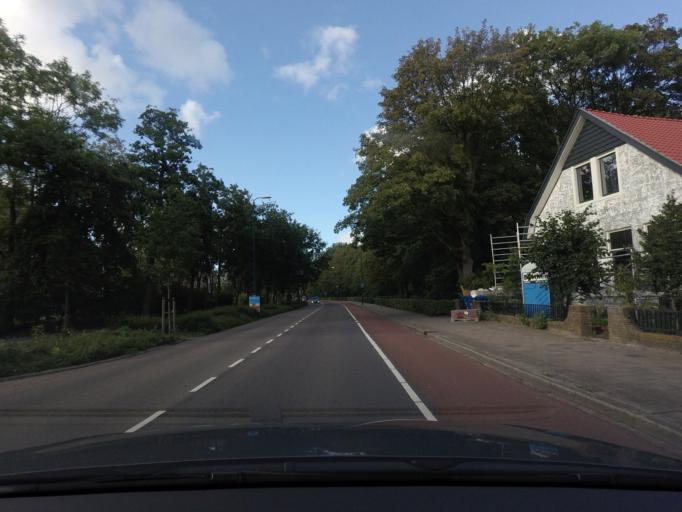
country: NL
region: South Holland
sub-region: Gemeente Oegstgeest
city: Oegstgeest
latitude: 52.1813
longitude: 4.4656
